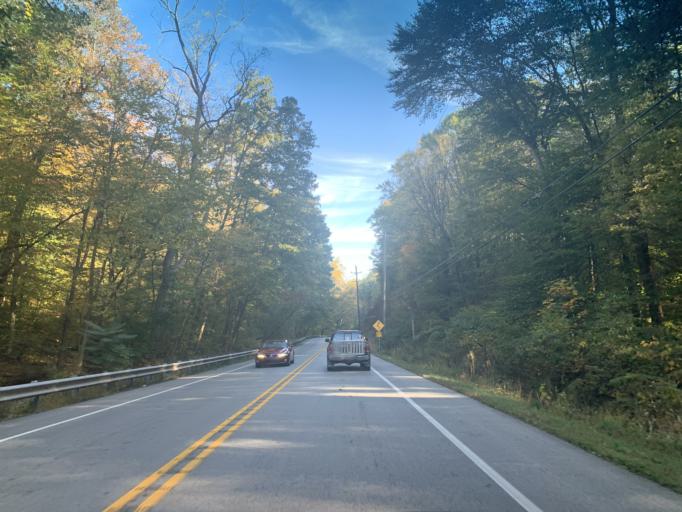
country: US
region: Pennsylvania
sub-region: Chester County
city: Parkesburg
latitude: 39.9485
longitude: -75.9137
